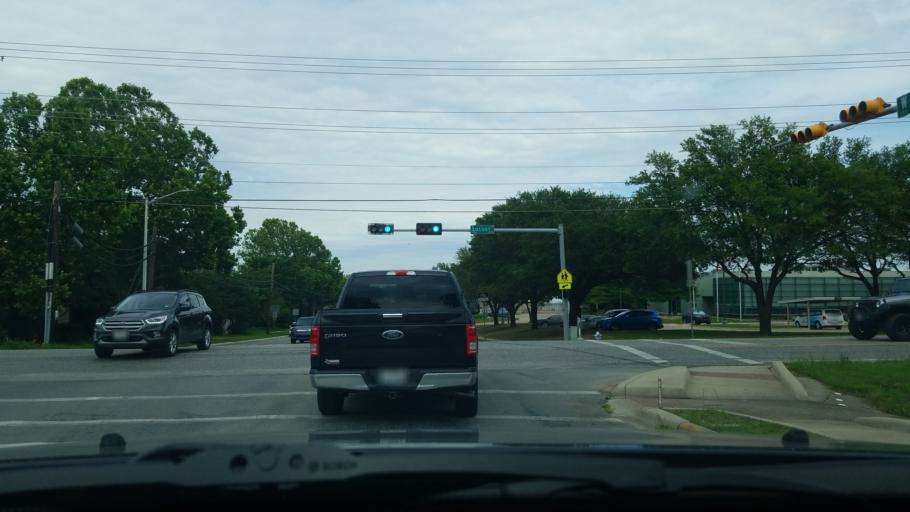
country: US
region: Texas
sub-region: Denton County
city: Denton
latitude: 33.2442
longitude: -97.1320
